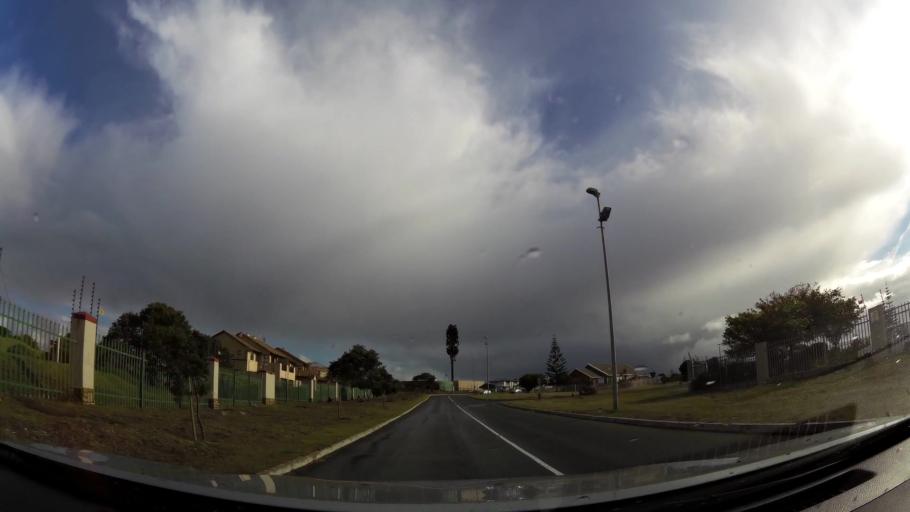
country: ZA
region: Western Cape
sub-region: Eden District Municipality
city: Mossel Bay
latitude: -34.1881
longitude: 22.1256
